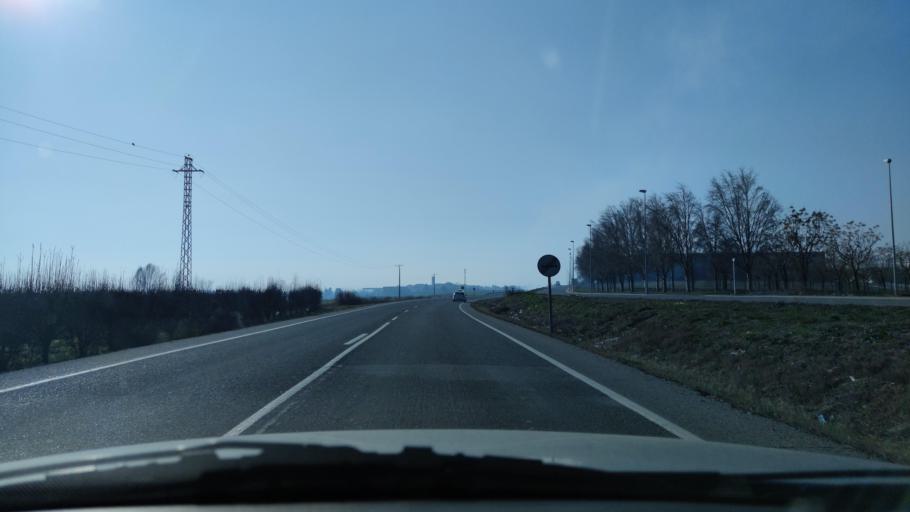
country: ES
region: Catalonia
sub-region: Provincia de Lleida
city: Torrefarrera
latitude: 41.6821
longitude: 0.6321
